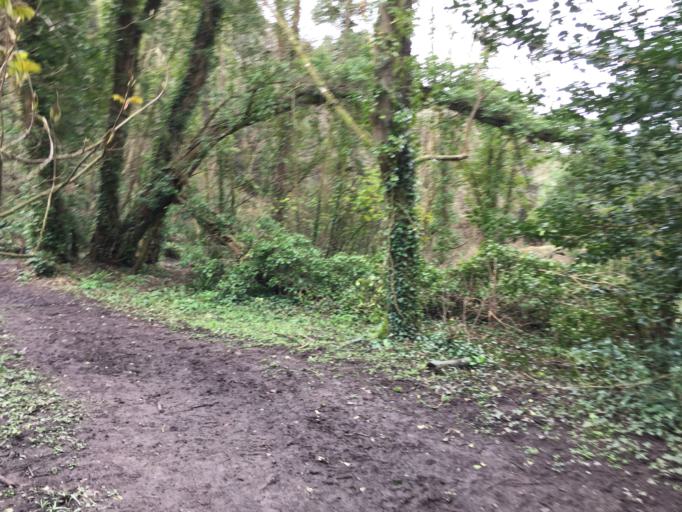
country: JE
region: St Helier
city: Saint Helier
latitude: 49.2121
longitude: -2.1330
